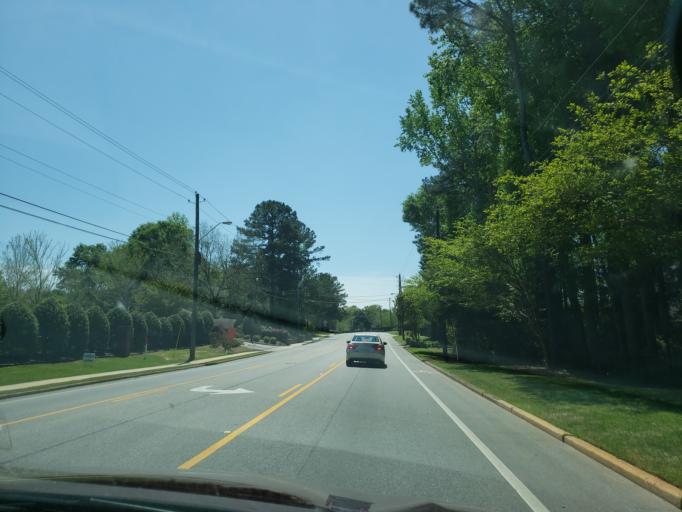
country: US
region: Alabama
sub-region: Lee County
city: Auburn
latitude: 32.6256
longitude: -85.4948
